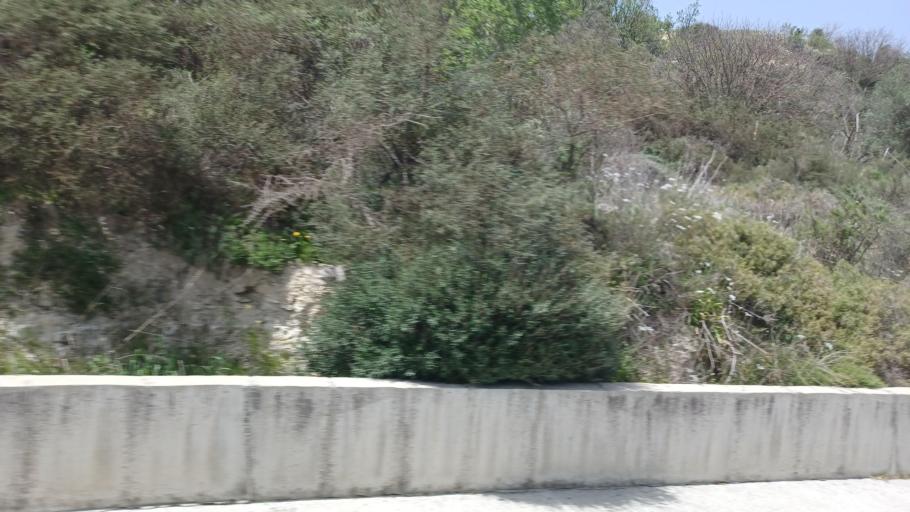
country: CY
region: Limassol
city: Pachna
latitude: 34.7821
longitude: 32.7421
